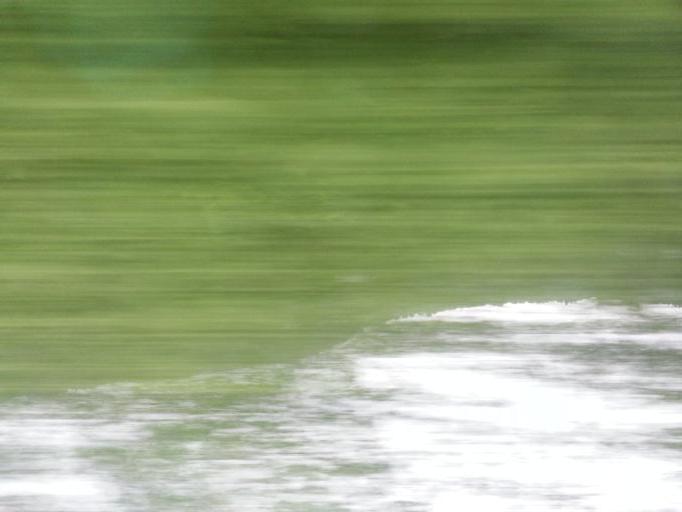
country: NO
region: Sor-Trondelag
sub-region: Melhus
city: Melhus
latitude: 63.2767
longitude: 10.2872
